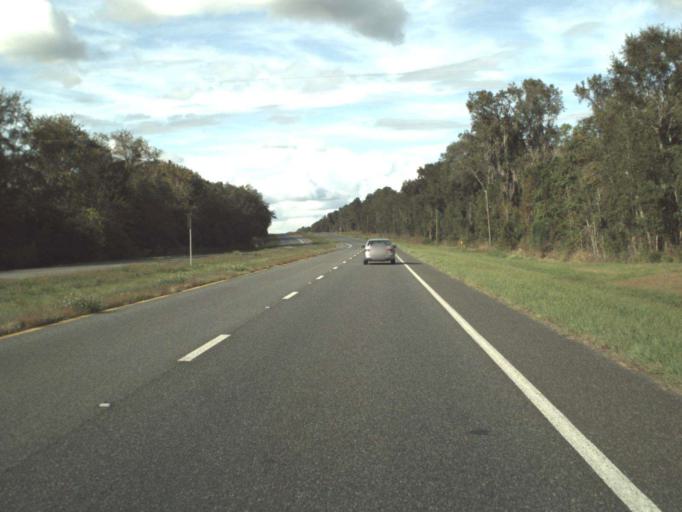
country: US
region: Florida
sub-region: Jefferson County
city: Monticello
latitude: 30.6325
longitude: -83.8729
